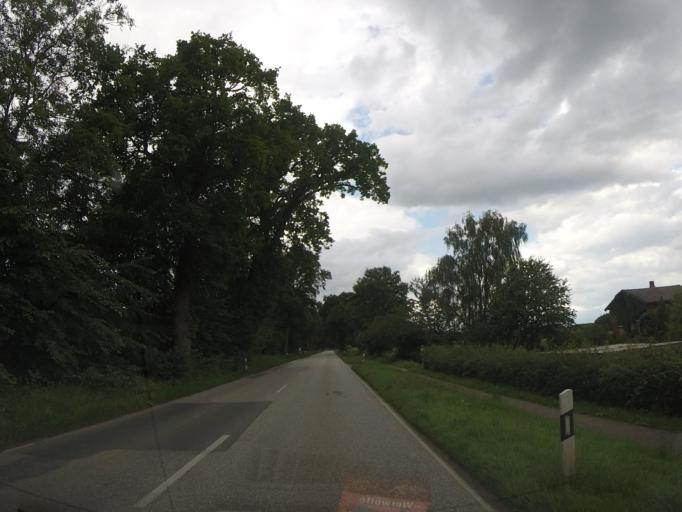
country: DE
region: Schleswig-Holstein
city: Ratekau
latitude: 53.9657
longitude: 10.7184
